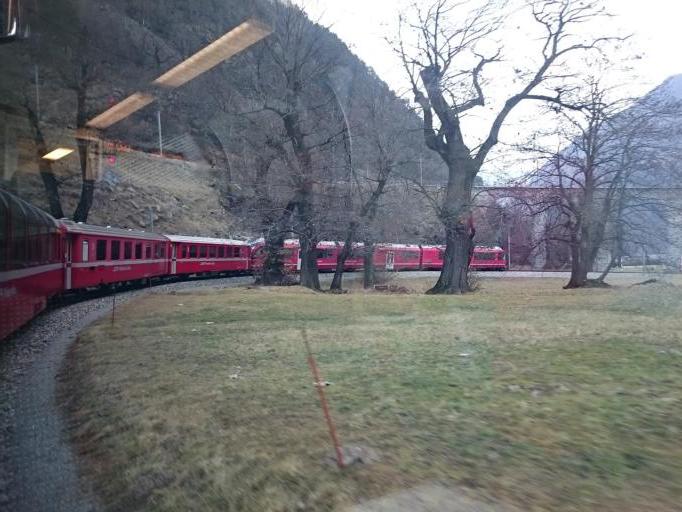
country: CH
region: Grisons
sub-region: Bernina District
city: Brusio
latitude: 46.2547
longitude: 10.1280
